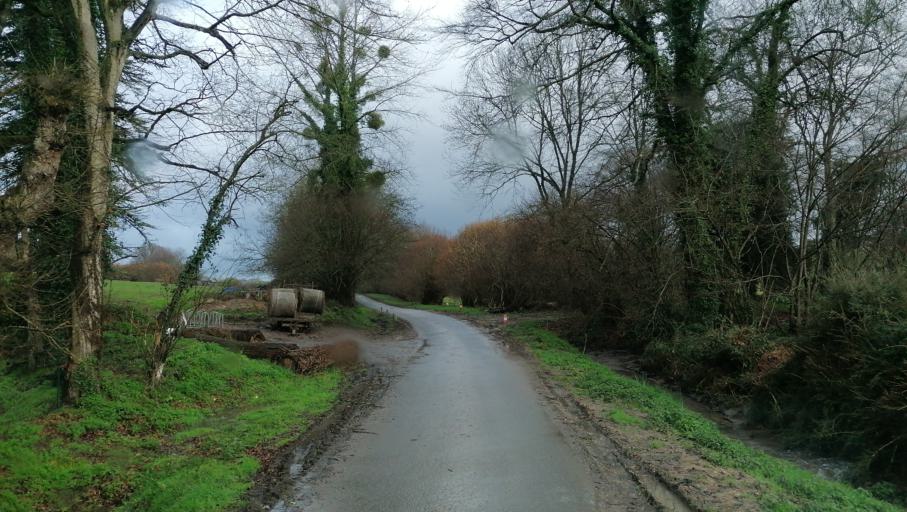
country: FR
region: Brittany
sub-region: Departement des Cotes-d'Armor
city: Plouagat
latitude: 48.4917
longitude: -2.9636
